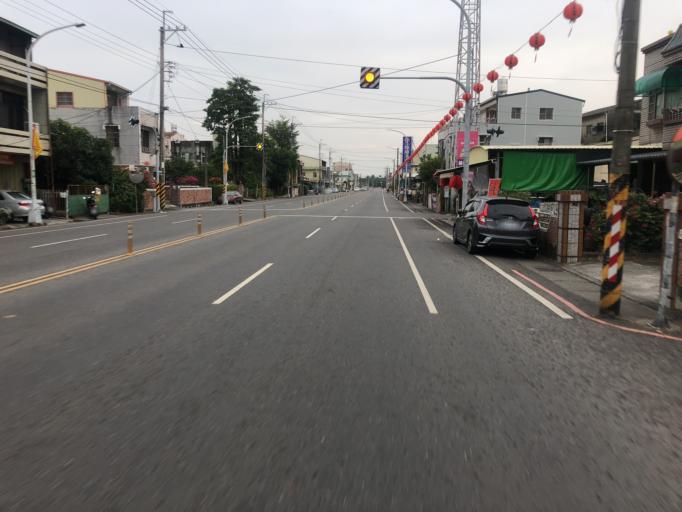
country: TW
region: Taiwan
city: Xinying
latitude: 23.1514
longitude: 120.2873
